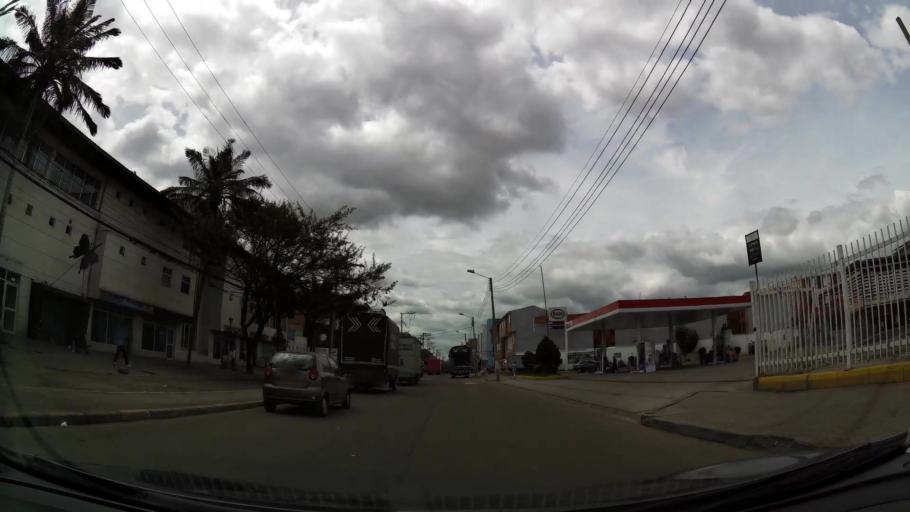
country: CO
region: Cundinamarca
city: Funza
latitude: 4.7097
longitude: -74.1392
